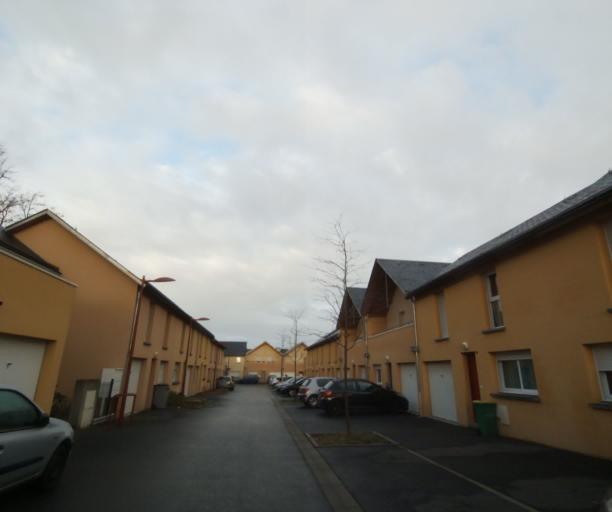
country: FR
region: Pays de la Loire
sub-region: Departement de la Sarthe
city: Le Mans
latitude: 47.9773
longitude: 0.2233
